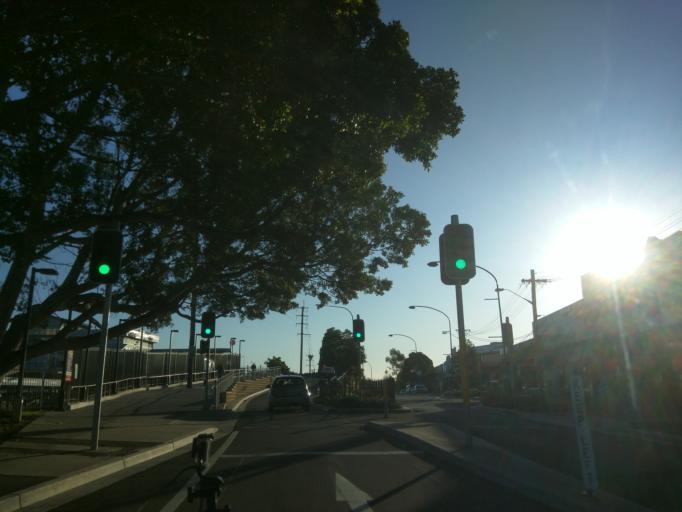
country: AU
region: New South Wales
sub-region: Sutherland Shire
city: Kirrawee
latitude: -34.0322
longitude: 151.0573
